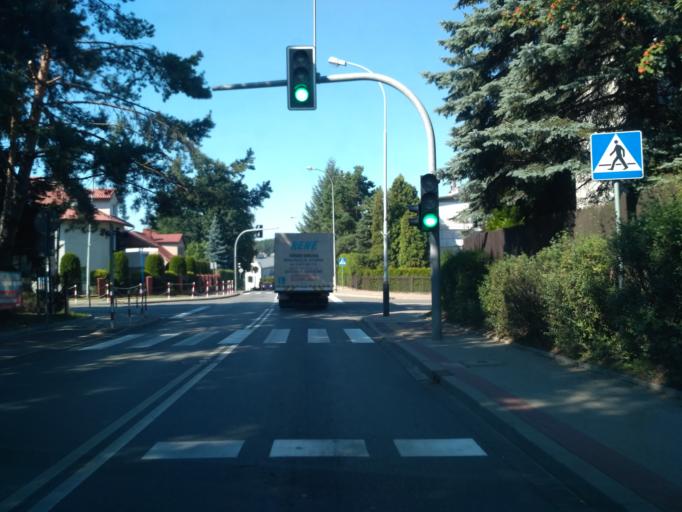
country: PL
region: Subcarpathian Voivodeship
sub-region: Krosno
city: Krosno
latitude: 49.6889
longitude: 21.7733
